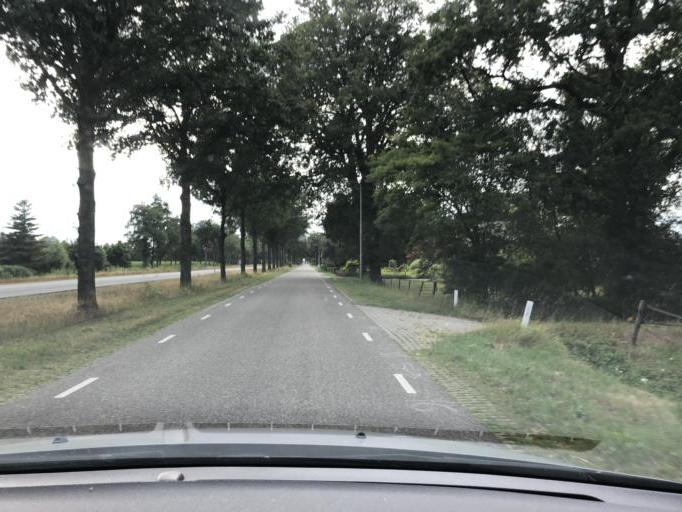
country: NL
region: Overijssel
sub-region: Gemeente Dalfsen
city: Dalfsen
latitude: 52.5915
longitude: 6.2967
